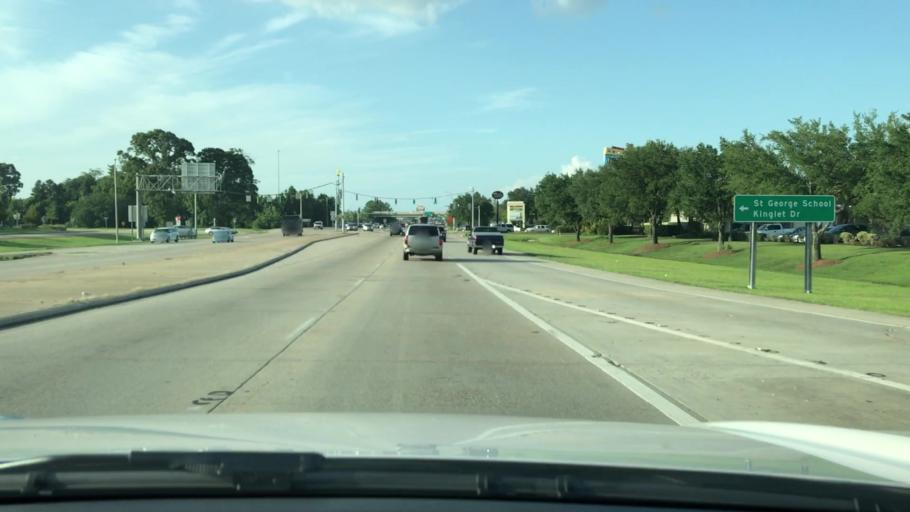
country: US
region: Louisiana
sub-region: East Baton Rouge Parish
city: Village Saint George
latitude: 30.3782
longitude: -91.0679
